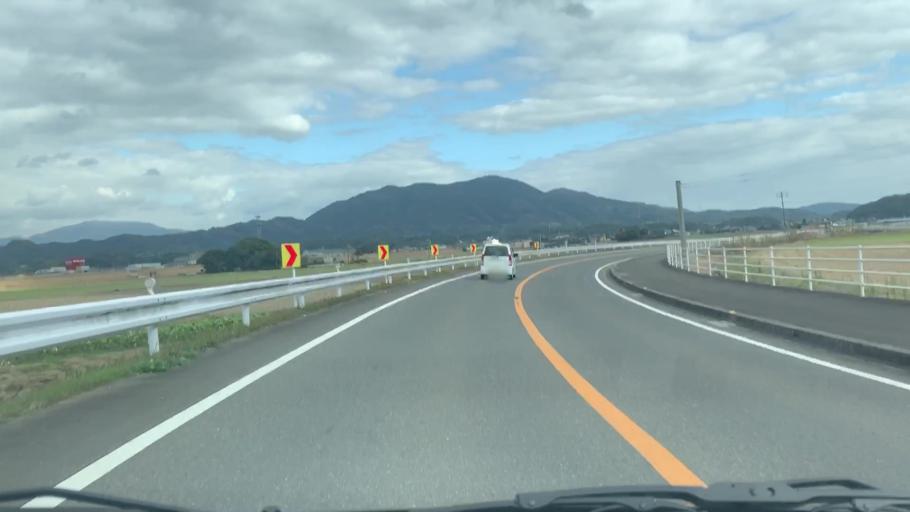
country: JP
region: Saga Prefecture
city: Takeocho-takeo
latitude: 33.2087
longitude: 130.0593
